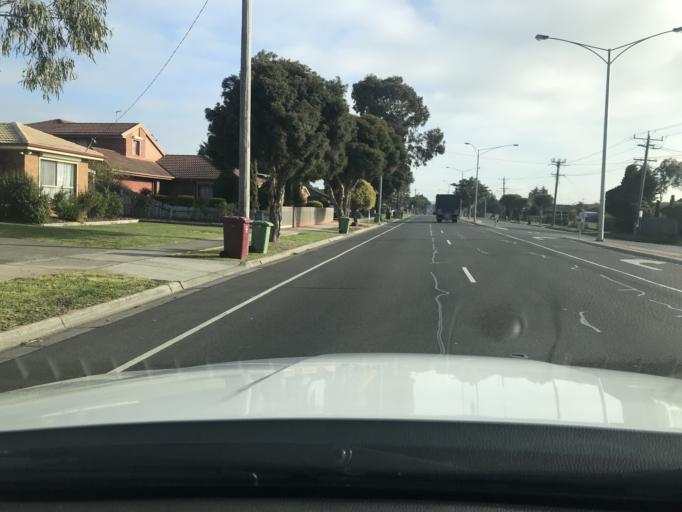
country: AU
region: Victoria
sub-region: Hume
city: Roxburgh Park
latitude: -37.6045
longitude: 144.9289
